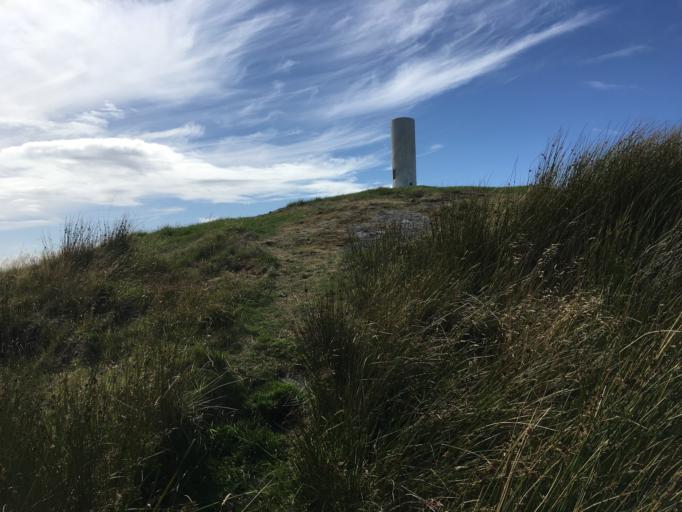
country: GB
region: Scotland
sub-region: Argyll and Bute
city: Isle Of Mull
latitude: 56.2570
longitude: -5.6449
